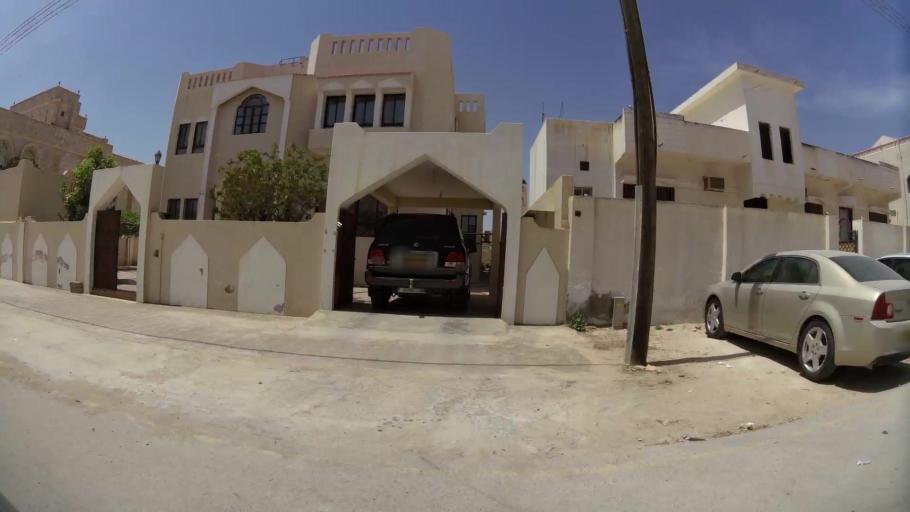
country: OM
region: Zufar
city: Salalah
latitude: 17.0641
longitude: 54.1592
